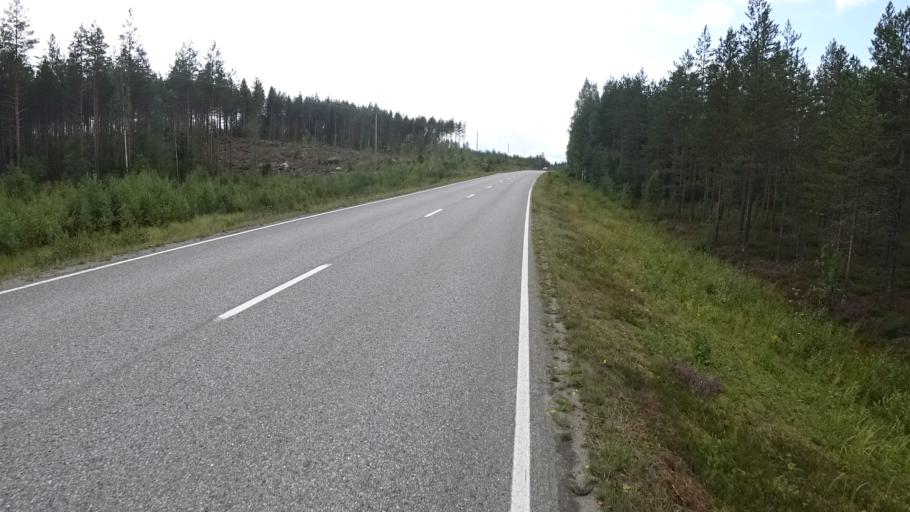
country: FI
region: North Karelia
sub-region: Joensuu
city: Ilomantsi
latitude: 62.6211
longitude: 31.2323
